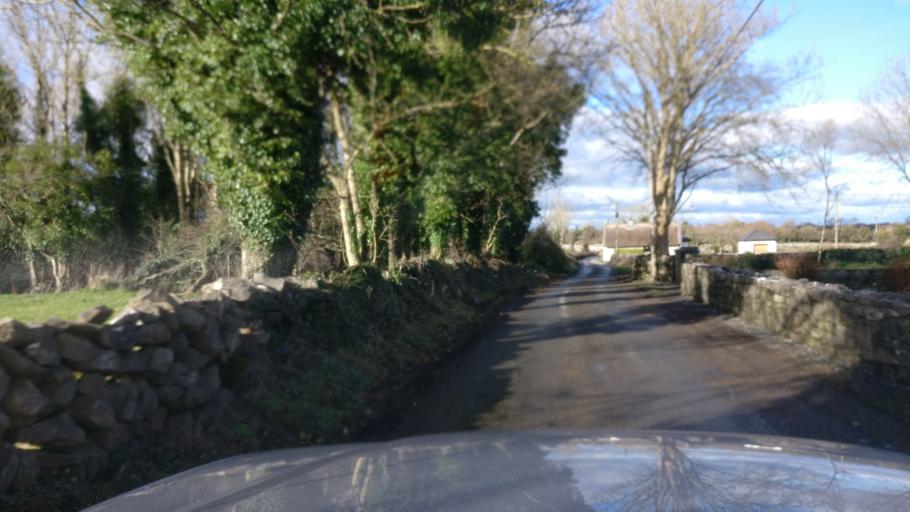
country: IE
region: Connaught
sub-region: County Galway
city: Athenry
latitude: 53.2279
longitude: -8.7992
